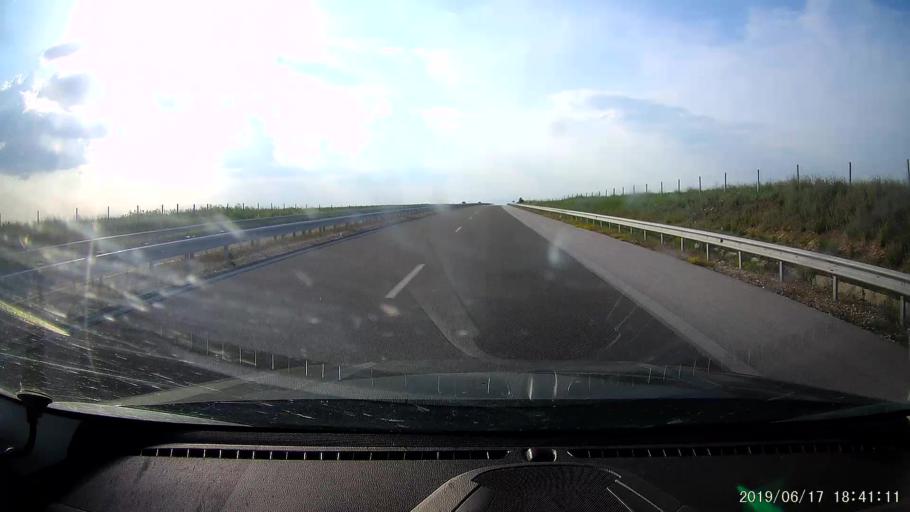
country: BG
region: Stara Zagora
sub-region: Obshtina Chirpan
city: Chirpan
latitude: 42.1676
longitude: 25.2603
